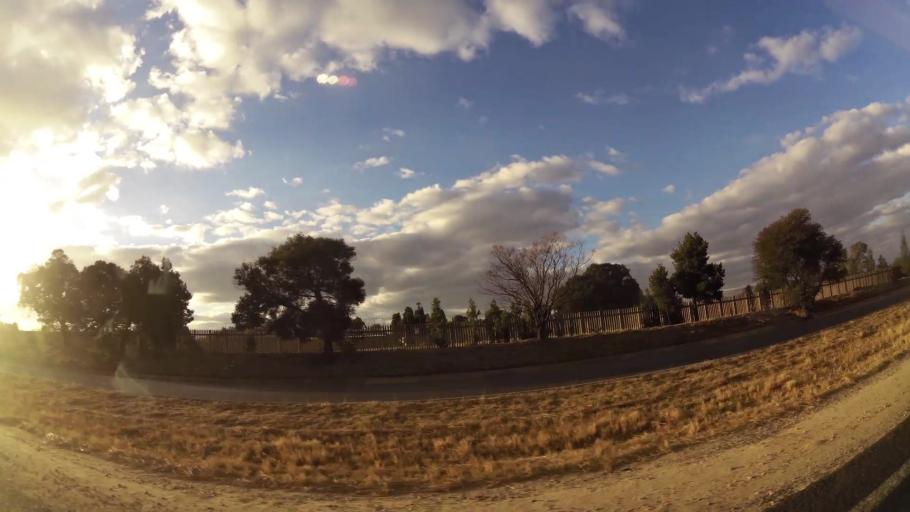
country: ZA
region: Gauteng
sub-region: City of Johannesburg Metropolitan Municipality
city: Midrand
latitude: -25.9475
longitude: 28.1577
